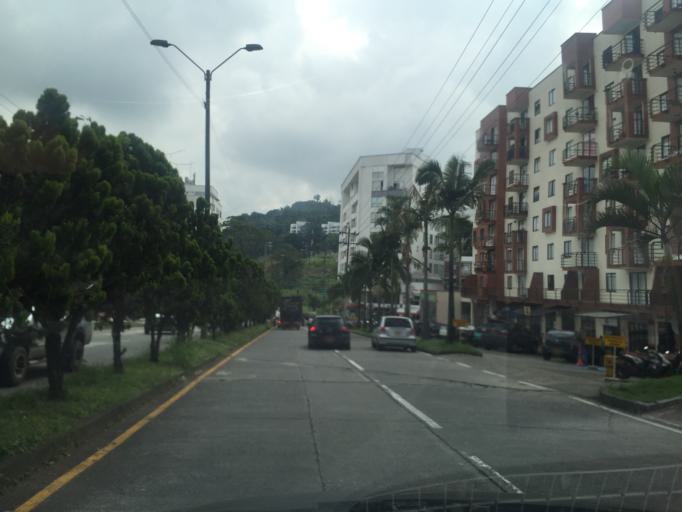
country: CO
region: Risaralda
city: Pereira
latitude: 4.8040
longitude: -75.6852
